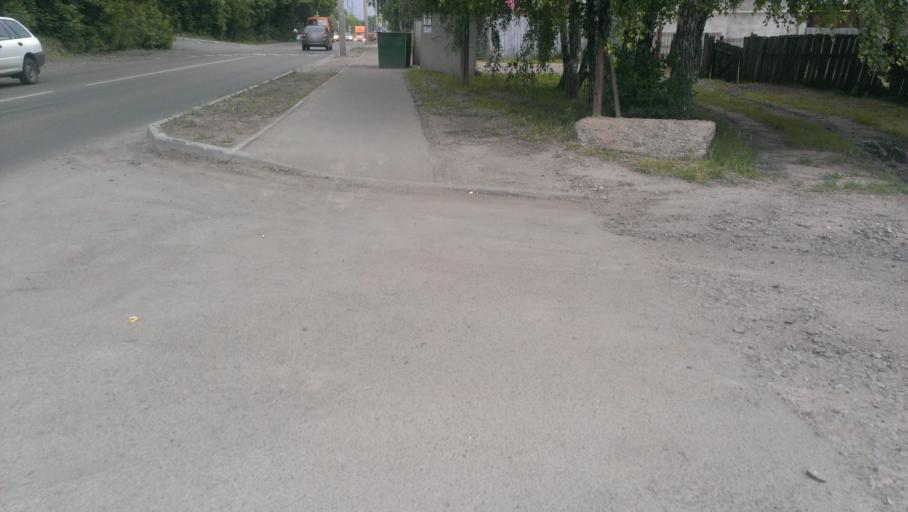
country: RU
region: Altai Krai
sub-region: Gorod Barnaulskiy
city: Barnaul
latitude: 53.3333
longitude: 83.7231
